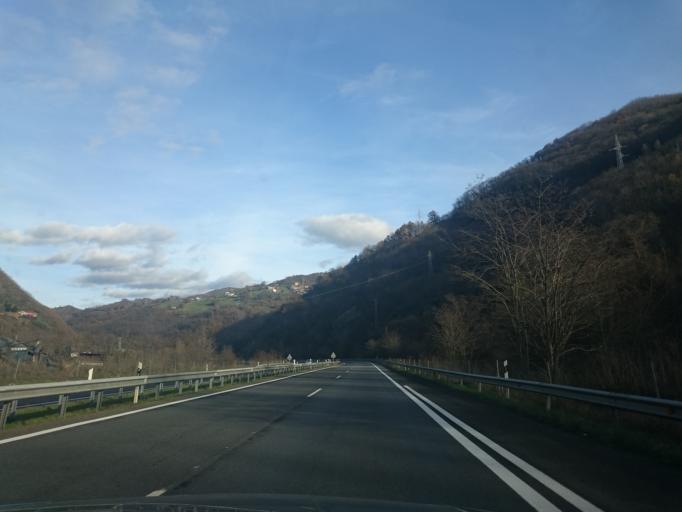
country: ES
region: Asturias
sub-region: Province of Asturias
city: Pola de Lena
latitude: 43.1844
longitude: -5.8046
